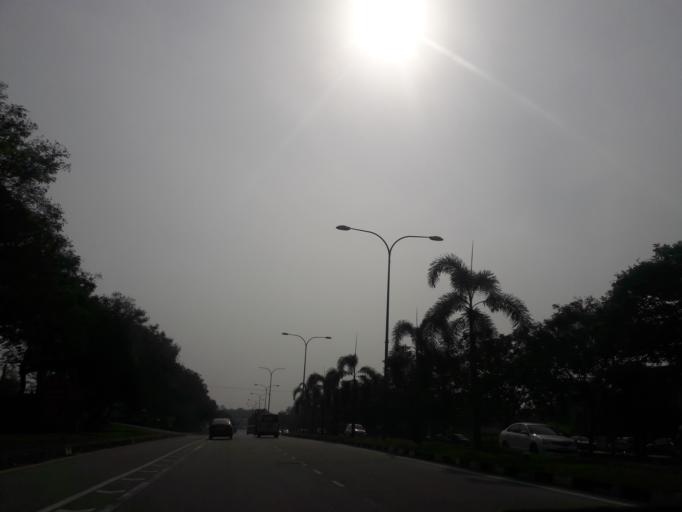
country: MY
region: Kedah
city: Kulim
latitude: 5.3505
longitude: 100.5273
